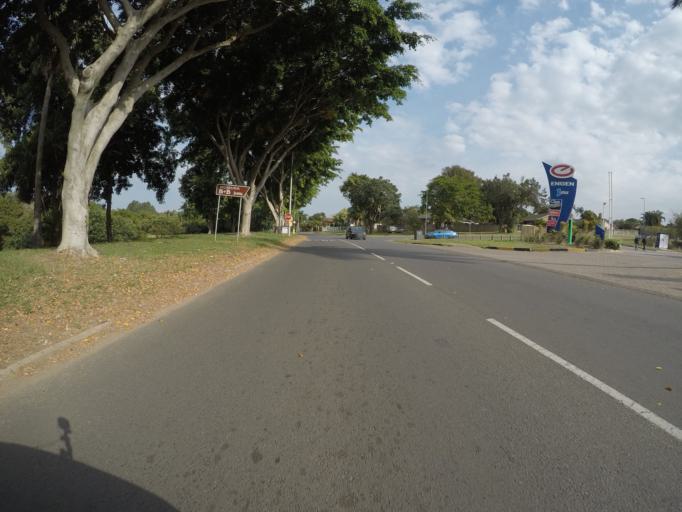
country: ZA
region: KwaZulu-Natal
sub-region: uThungulu District Municipality
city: Richards Bay
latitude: -28.7363
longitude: 32.0662
